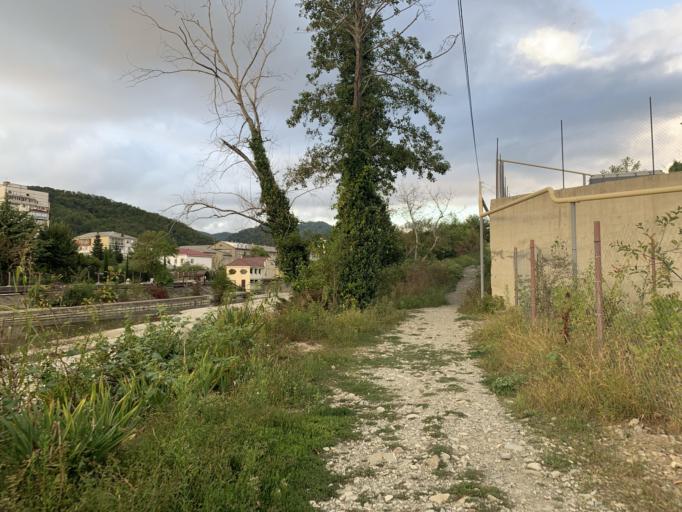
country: RU
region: Krasnodarskiy
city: Nebug
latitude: 44.1669
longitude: 39.0035
